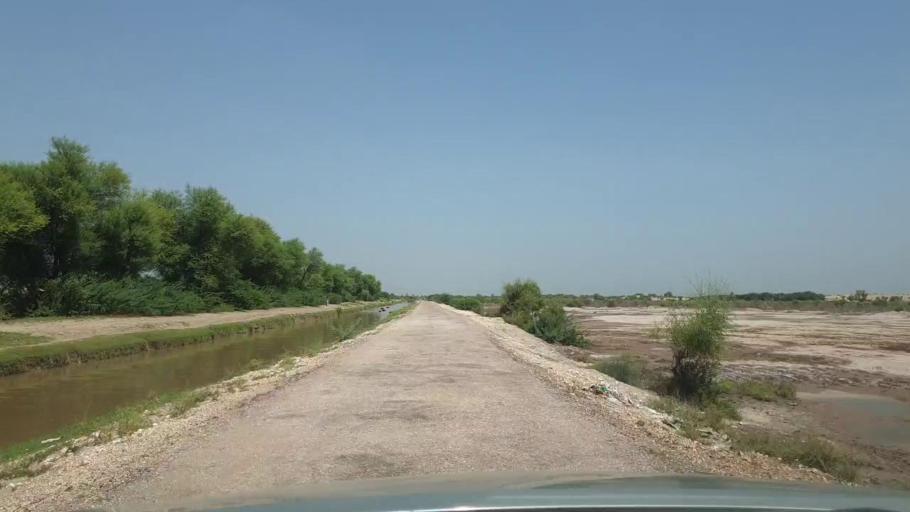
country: PK
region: Sindh
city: Rohri
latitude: 27.6181
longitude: 69.0988
